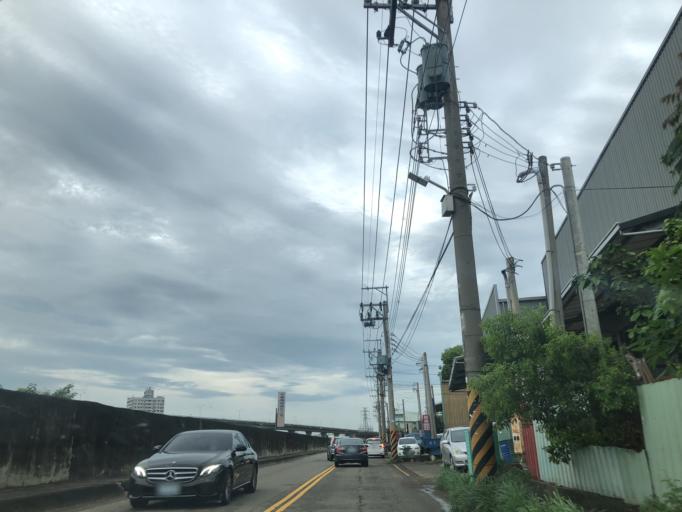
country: TW
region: Taiwan
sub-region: Taichung City
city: Taichung
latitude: 24.1211
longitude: 120.7034
